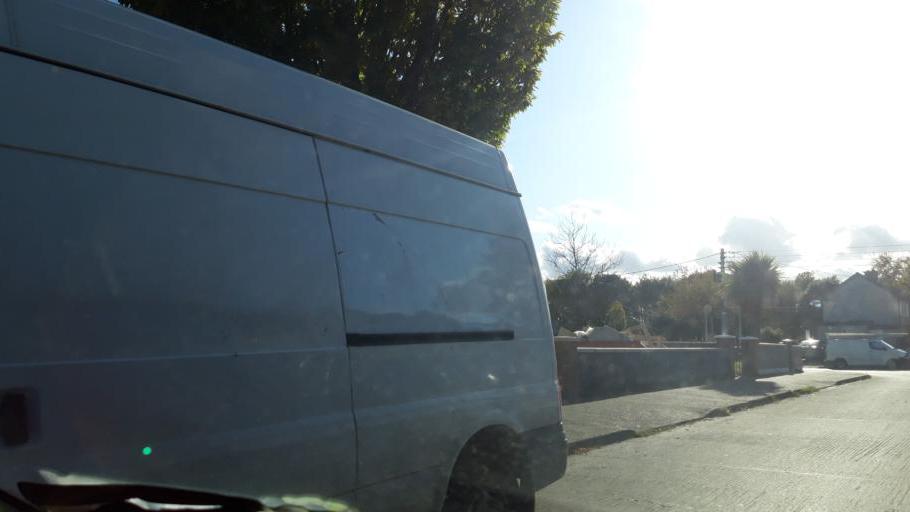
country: IE
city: Coolock
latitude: 53.3852
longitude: -6.1943
